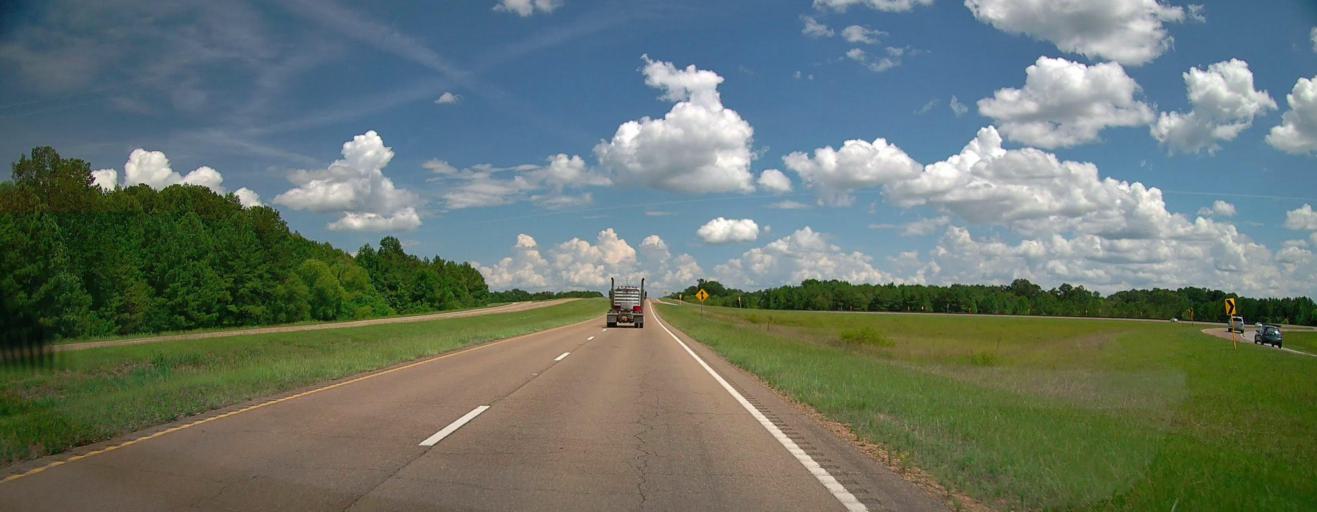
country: US
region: Mississippi
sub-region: Monroe County
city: Aberdeen
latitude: 33.8155
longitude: -88.4952
